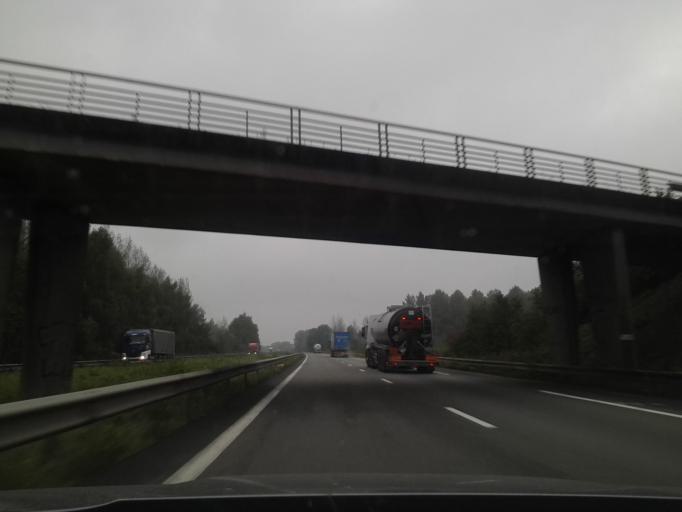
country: FR
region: Nord-Pas-de-Calais
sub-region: Departement du Nord
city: Crespin
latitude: 50.4225
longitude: 3.6365
